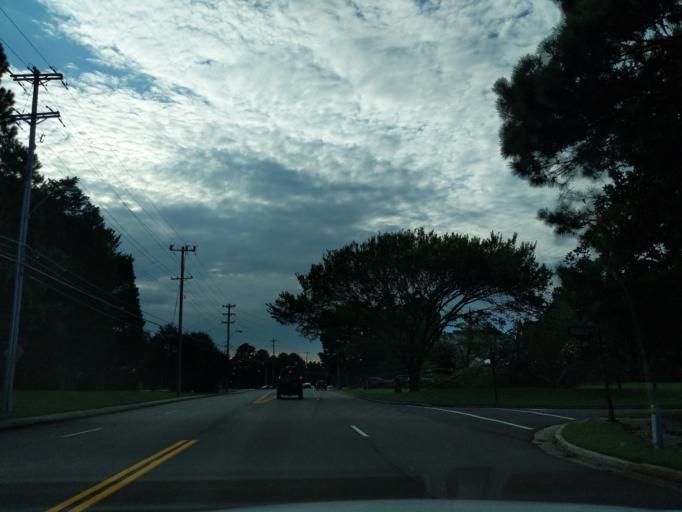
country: US
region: Tennessee
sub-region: Shelby County
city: Germantown
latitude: 35.0740
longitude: -89.7926
